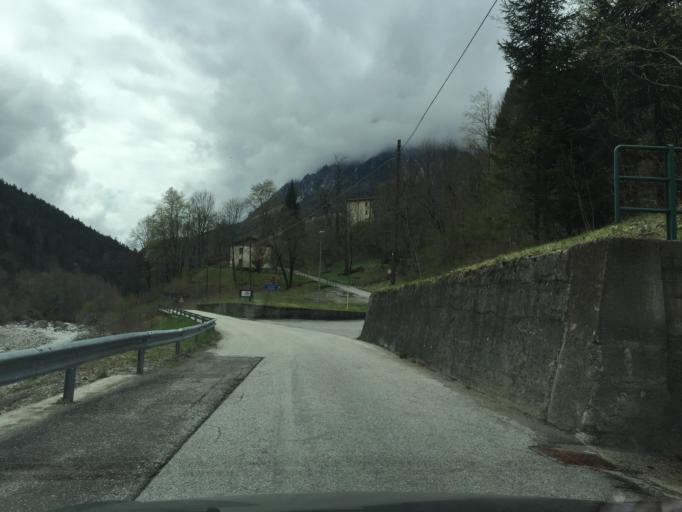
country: IT
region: Friuli Venezia Giulia
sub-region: Provincia di Udine
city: Moggio Udinese
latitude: 46.4886
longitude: 13.1949
